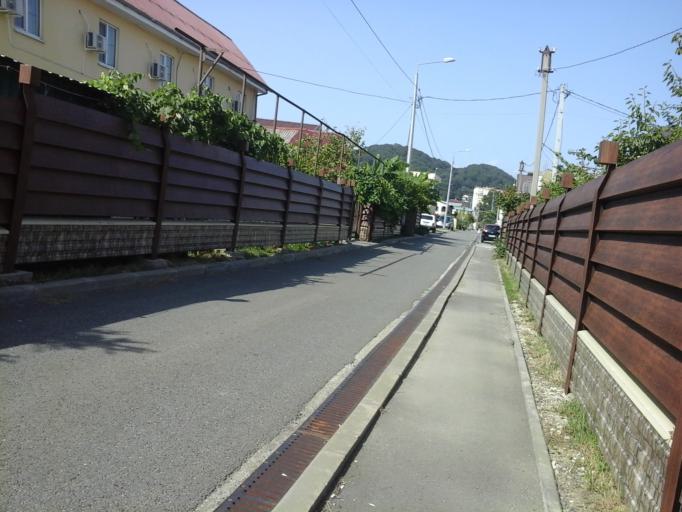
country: RU
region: Krasnodarskiy
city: Adler
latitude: 43.4107
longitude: 39.9565
